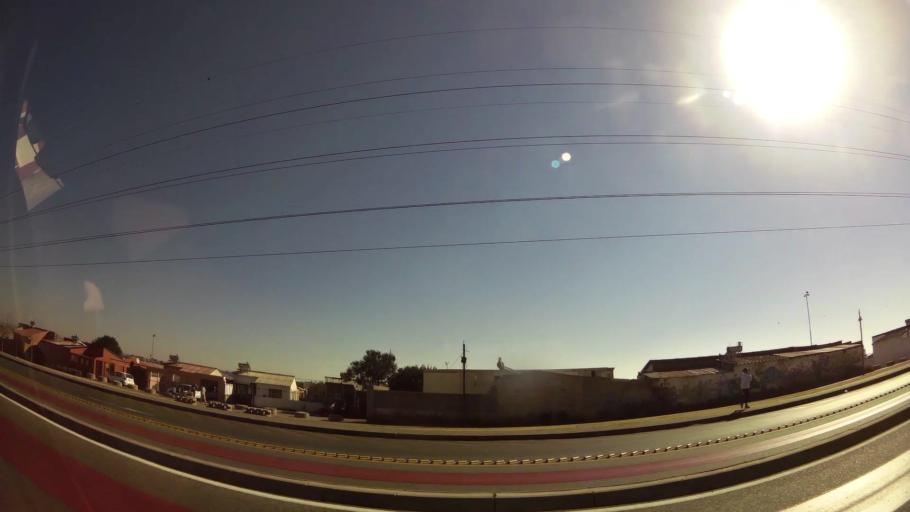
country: ZA
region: Gauteng
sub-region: City of Johannesburg Metropolitan Municipality
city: Johannesburg
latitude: -26.1871
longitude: 27.9747
